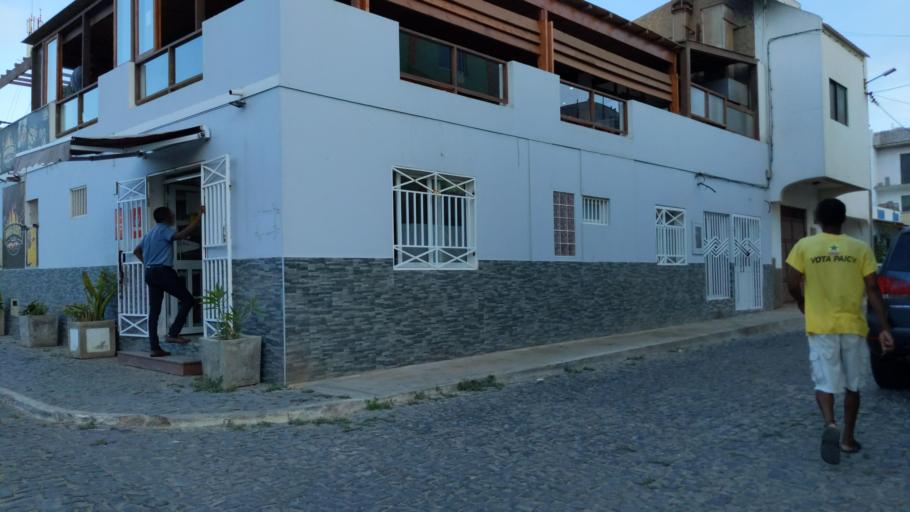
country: CV
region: Sal
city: Santa Maria
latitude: 16.5989
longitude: -22.9033
